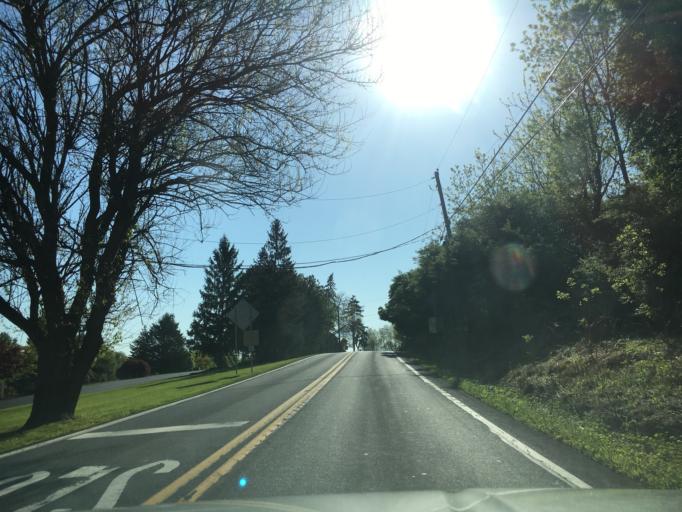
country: US
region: Pennsylvania
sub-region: Lehigh County
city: Catasauqua
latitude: 40.6748
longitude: -75.4313
